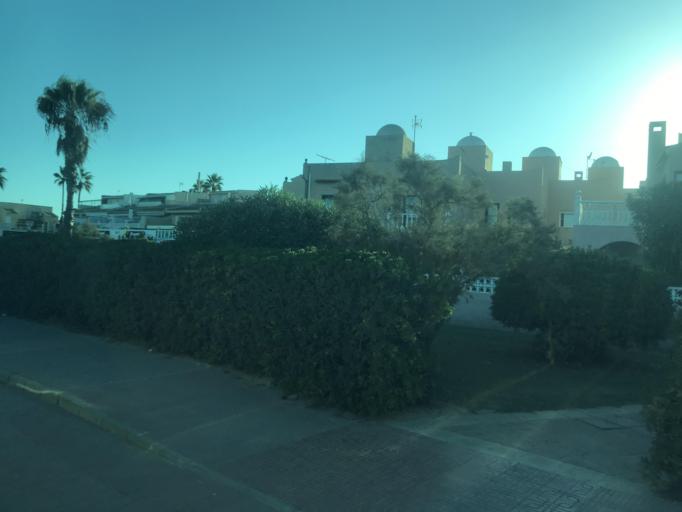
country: ES
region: Valencia
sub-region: Provincia de Alicante
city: Torrevieja
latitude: 37.9908
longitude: -0.6564
